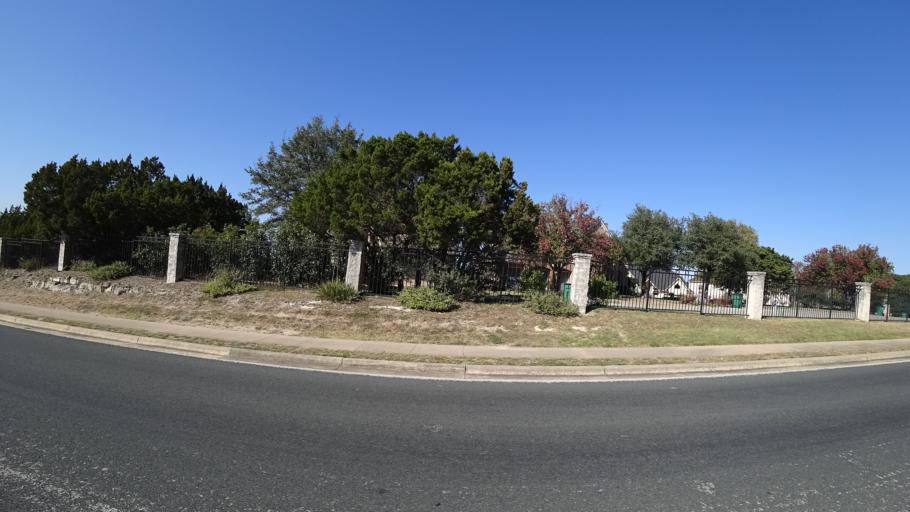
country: US
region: Texas
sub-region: Travis County
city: Lost Creek
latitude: 30.3718
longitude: -97.8575
